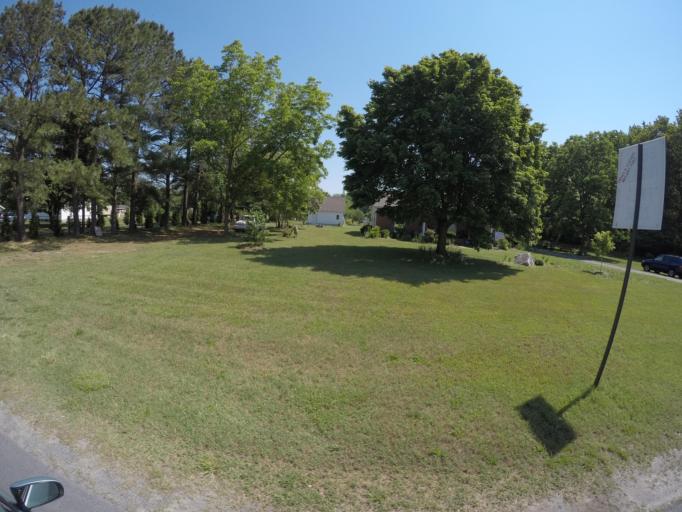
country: US
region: Delaware
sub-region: Sussex County
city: Georgetown
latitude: 38.6965
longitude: -75.3650
